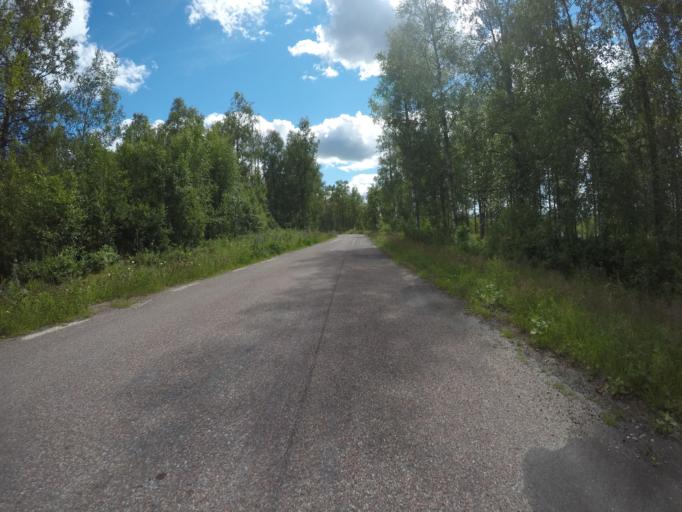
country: SE
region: OErebro
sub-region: Hallefors Kommun
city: Haellefors
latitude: 60.0485
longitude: 14.5053
